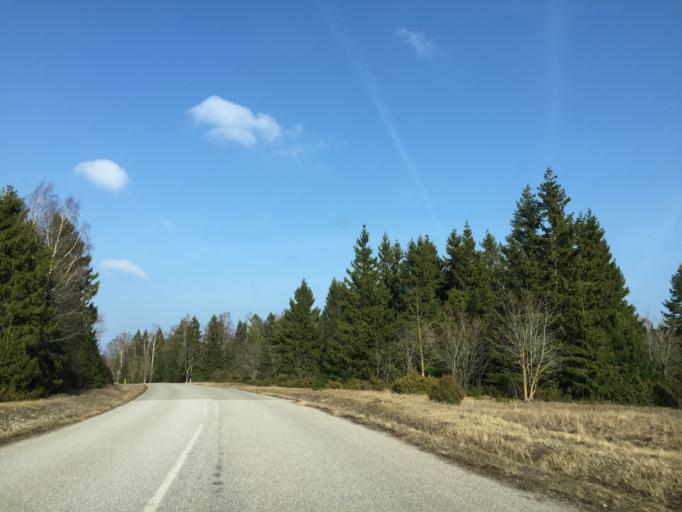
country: EE
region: Saare
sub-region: Kuressaare linn
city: Kuressaare
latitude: 58.0487
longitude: 22.1296
